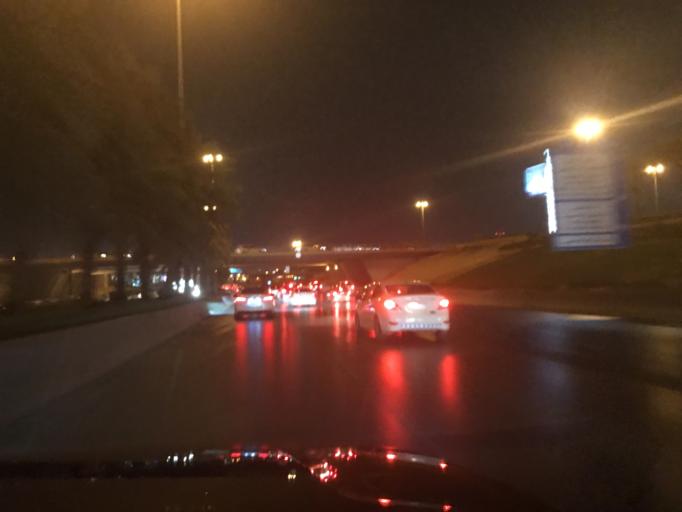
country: SA
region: Ar Riyad
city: Riyadh
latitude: 24.7157
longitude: 46.7611
